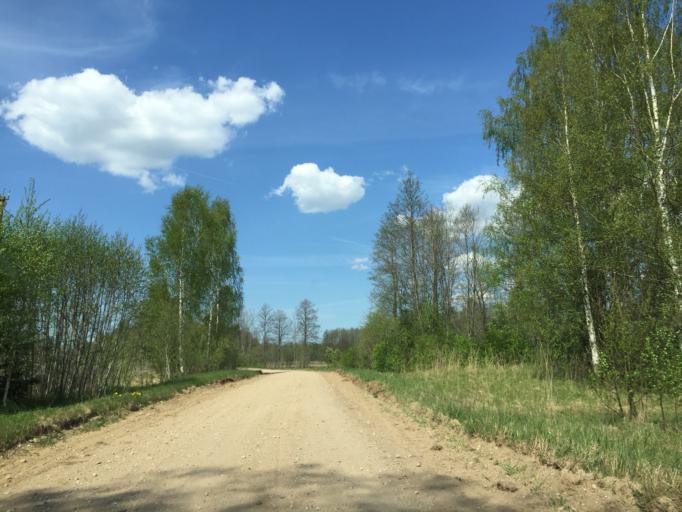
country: LV
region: Limbazu Rajons
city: Limbazi
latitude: 57.3836
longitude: 24.6099
